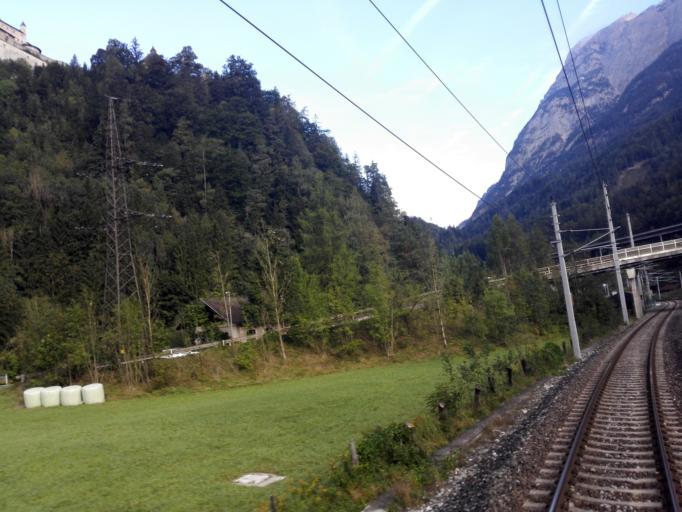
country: AT
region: Salzburg
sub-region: Politischer Bezirk Sankt Johann im Pongau
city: Werfen
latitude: 47.4815
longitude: 13.1922
